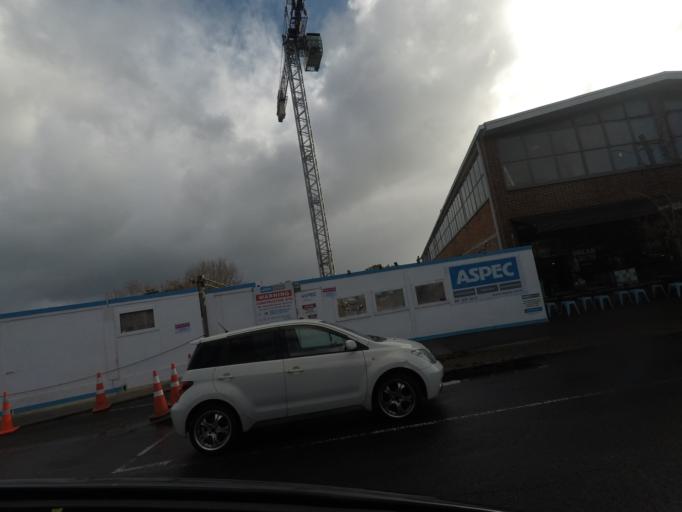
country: NZ
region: Auckland
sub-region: Auckland
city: Auckland
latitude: -36.8567
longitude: 174.7460
